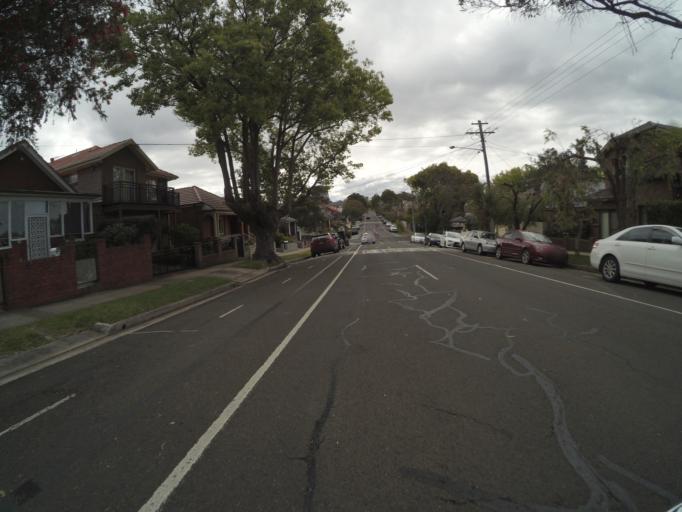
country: AU
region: New South Wales
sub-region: Canada Bay
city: Drummoyne
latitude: -33.8527
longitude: 151.1572
